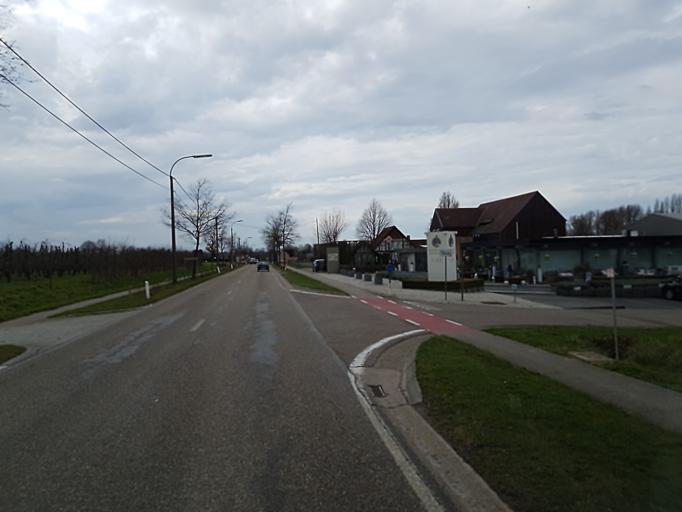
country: BE
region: Flanders
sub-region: Provincie Limburg
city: Nieuwerkerken
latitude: 50.9197
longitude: 5.2321
